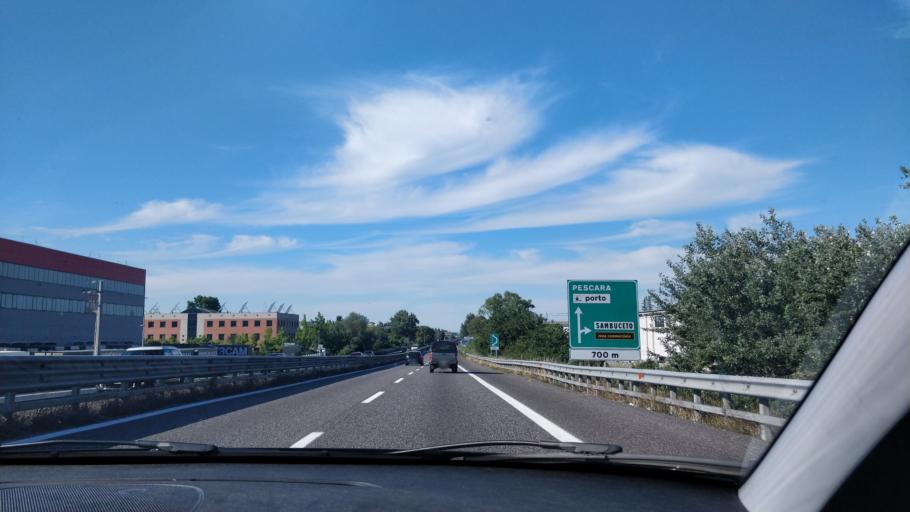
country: IT
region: Abruzzo
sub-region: Provincia di Pescara
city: Santa Teresa
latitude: 42.4111
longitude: 14.1635
